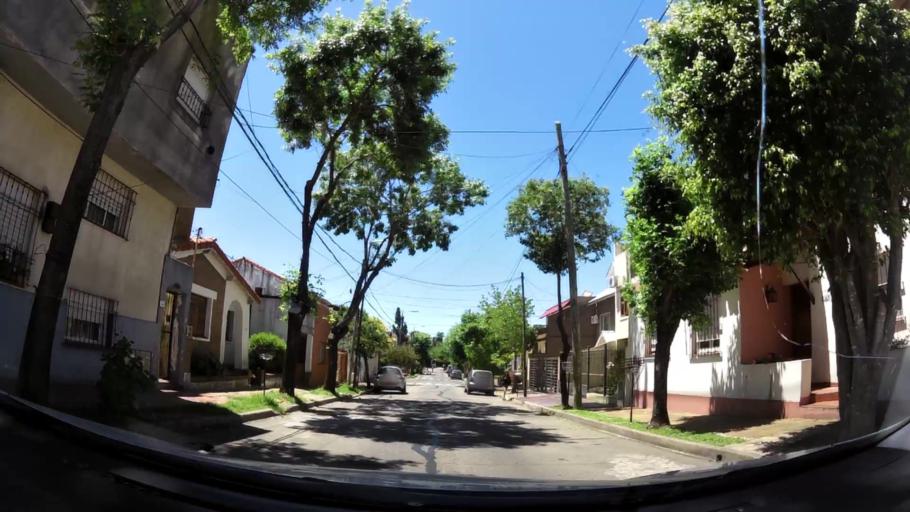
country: AR
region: Buenos Aires
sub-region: Partido de Tigre
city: Tigre
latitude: -34.4435
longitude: -58.5472
